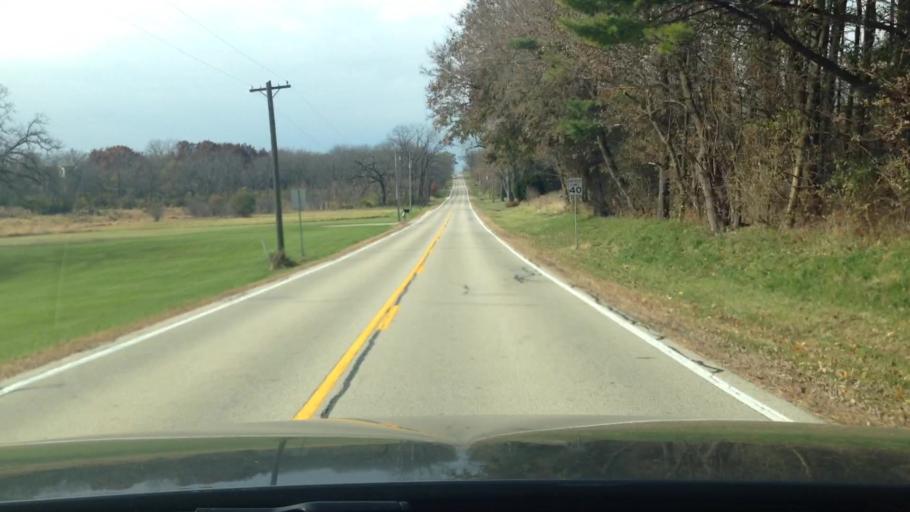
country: US
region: Illinois
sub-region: McHenry County
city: Woodstock
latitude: 42.2984
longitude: -88.4606
